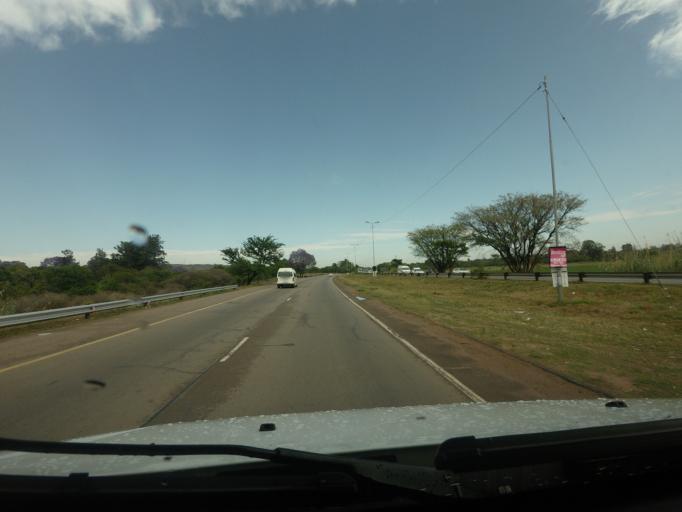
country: ZA
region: Gauteng
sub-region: City of Tshwane Metropolitan Municipality
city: Pretoria
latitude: -25.6859
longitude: 28.2905
